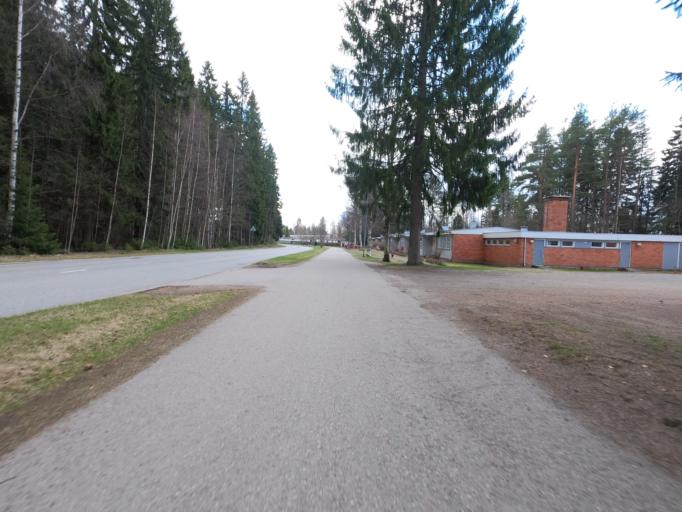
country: FI
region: North Karelia
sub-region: Joensuu
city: Joensuu
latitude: 62.5847
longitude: 29.7781
